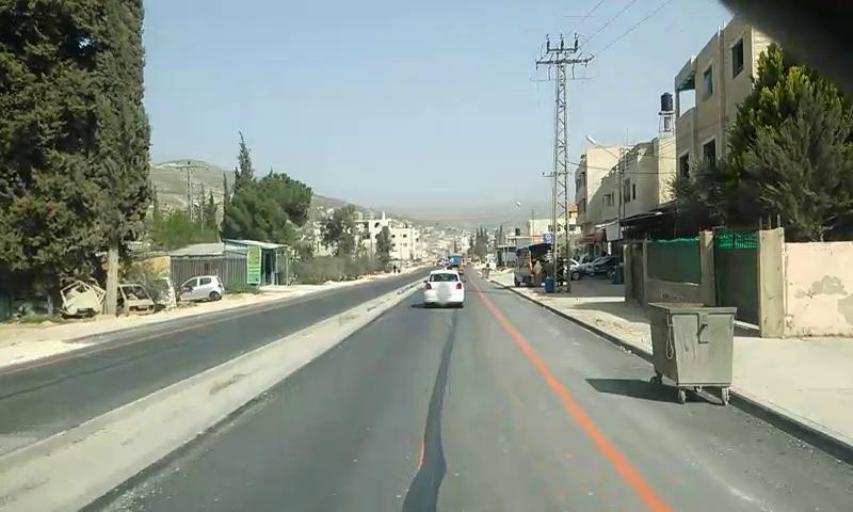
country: PS
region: West Bank
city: Huwwarah
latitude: 32.1405
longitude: 35.2580
